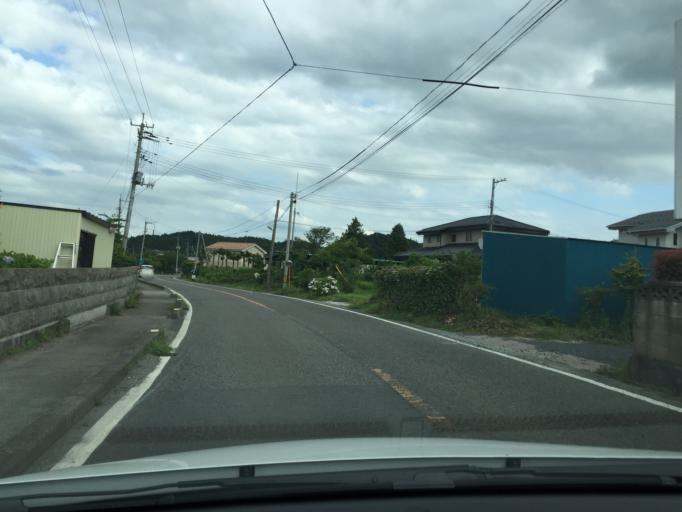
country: JP
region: Tochigi
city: Kuroiso
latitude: 37.1760
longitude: 140.1526
